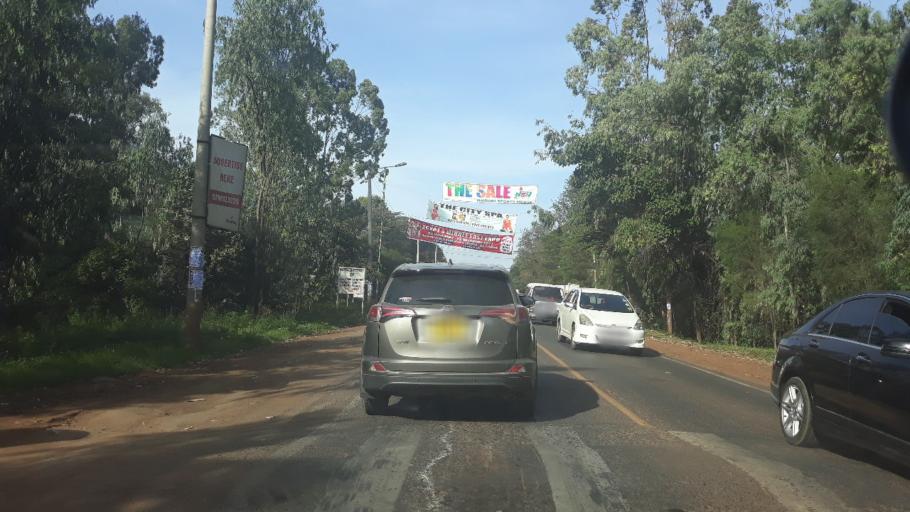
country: KE
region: Nairobi Area
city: Pumwani
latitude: -1.2516
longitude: 36.8459
